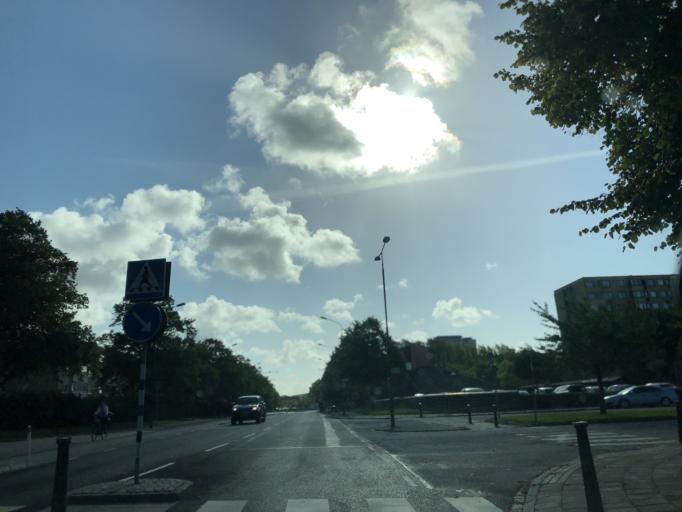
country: SE
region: Skane
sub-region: Malmo
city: Malmoe
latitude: 55.5843
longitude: 12.9764
